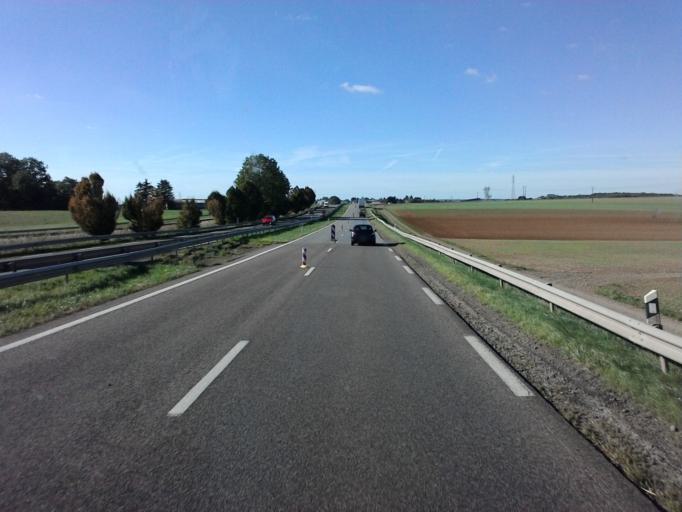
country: FR
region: Lorraine
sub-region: Departement de Meurthe-et-Moselle
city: Villers-la-Montagne
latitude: 49.4781
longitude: 5.8238
